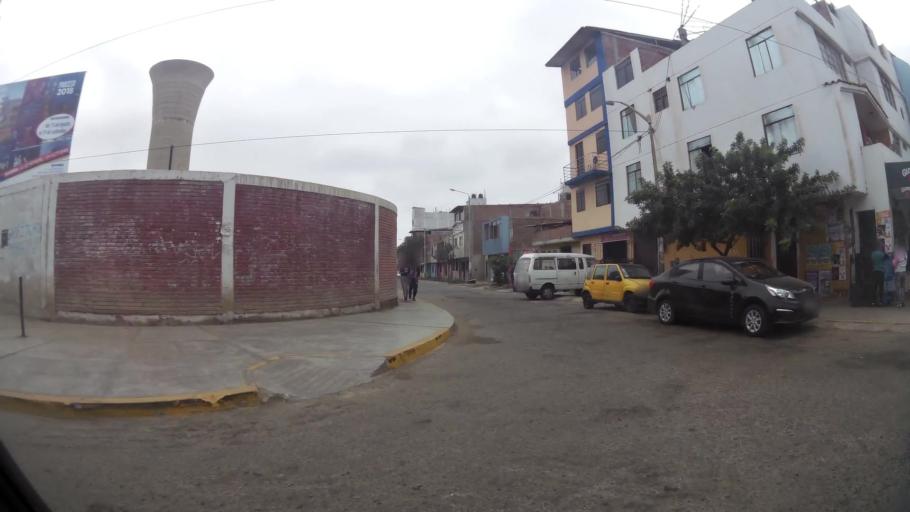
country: PE
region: La Libertad
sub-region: Provincia de Trujillo
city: Trujillo
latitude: -8.1099
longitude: -79.0383
